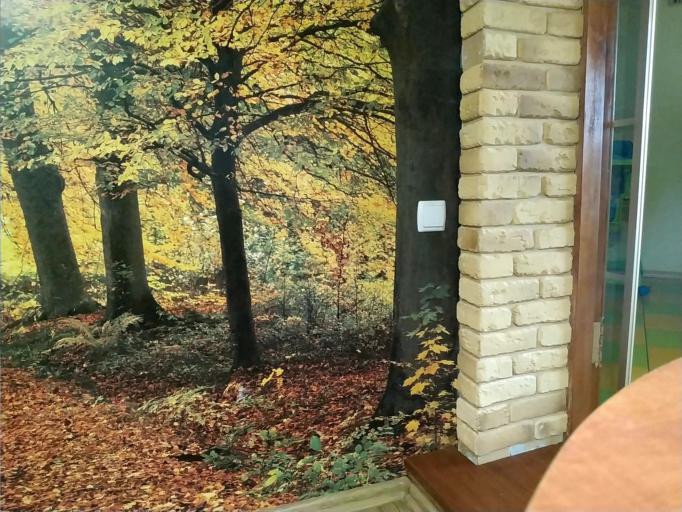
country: RU
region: Smolensk
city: Dorogobuzh
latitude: 54.9164
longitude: 33.3297
